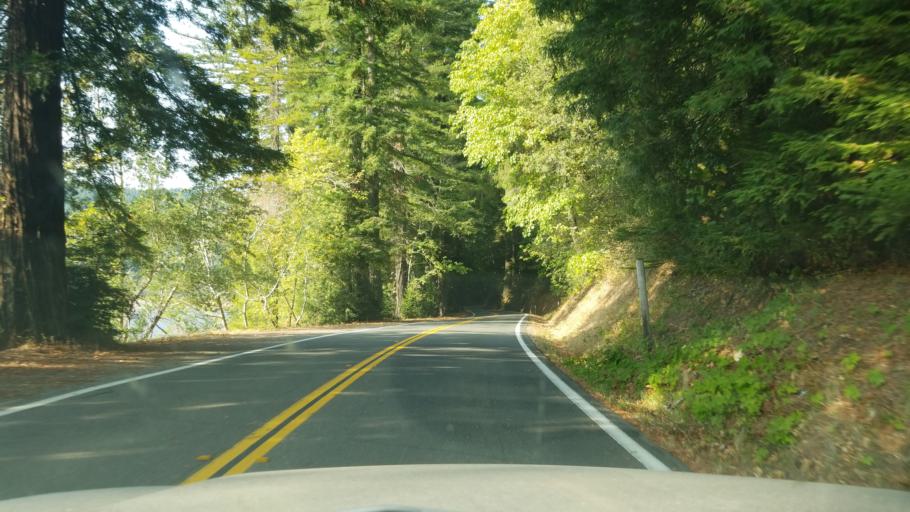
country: US
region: California
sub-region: Humboldt County
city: Redway
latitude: 40.2488
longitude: -123.8231
